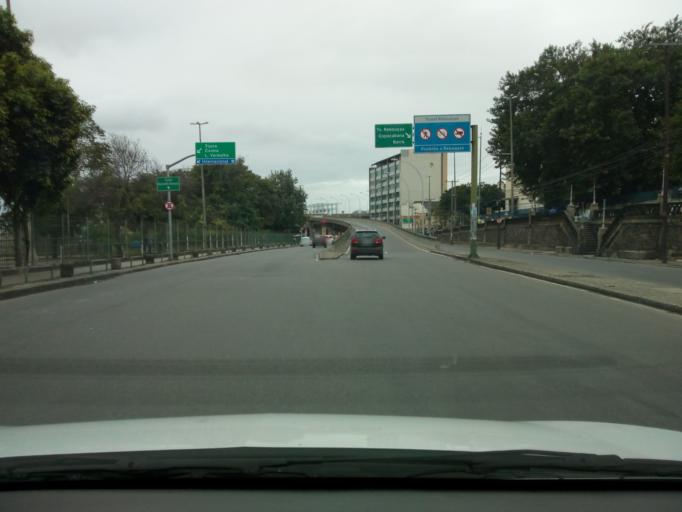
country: BR
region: Rio de Janeiro
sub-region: Rio De Janeiro
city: Rio de Janeiro
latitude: -22.8992
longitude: -43.2221
